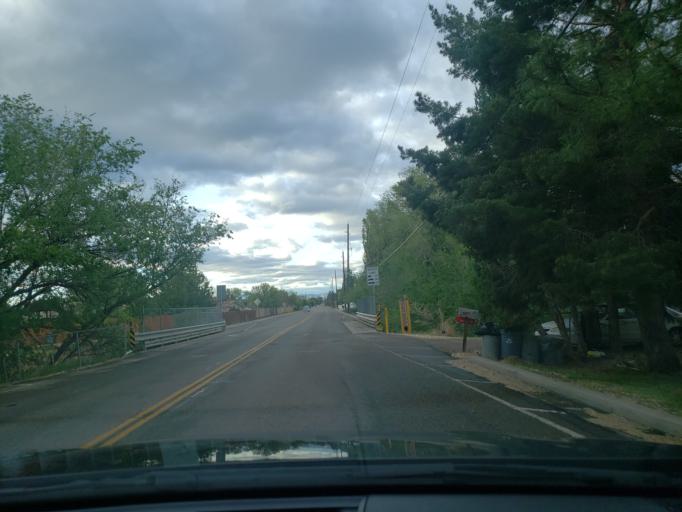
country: US
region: Colorado
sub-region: Mesa County
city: Fruita
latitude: 39.1675
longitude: -108.7290
